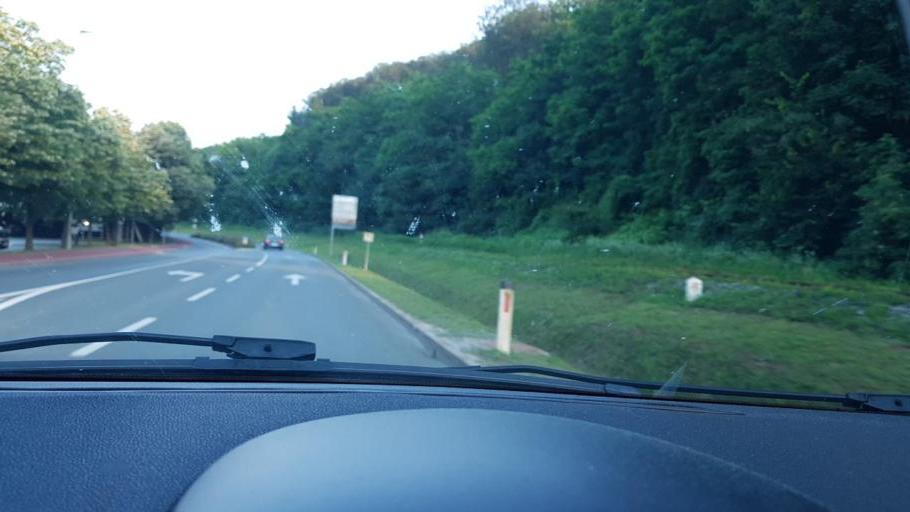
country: SI
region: Rogaska Slatina
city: Rogaska Slatina
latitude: 46.2385
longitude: 15.6330
